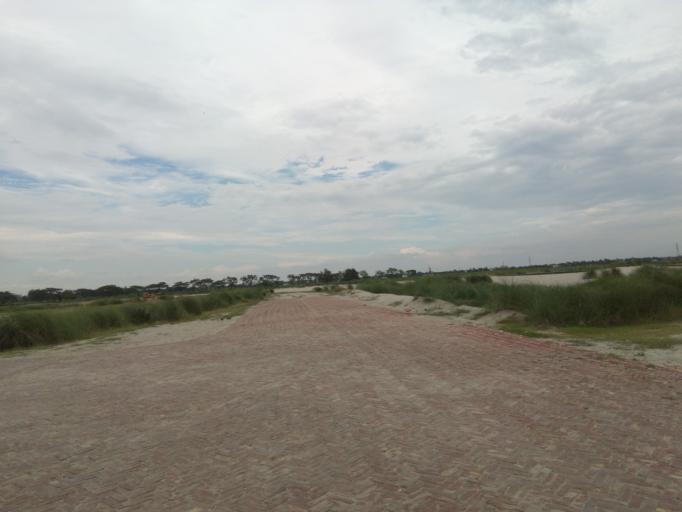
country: BD
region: Dhaka
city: Paltan
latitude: 23.7279
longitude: 90.4553
